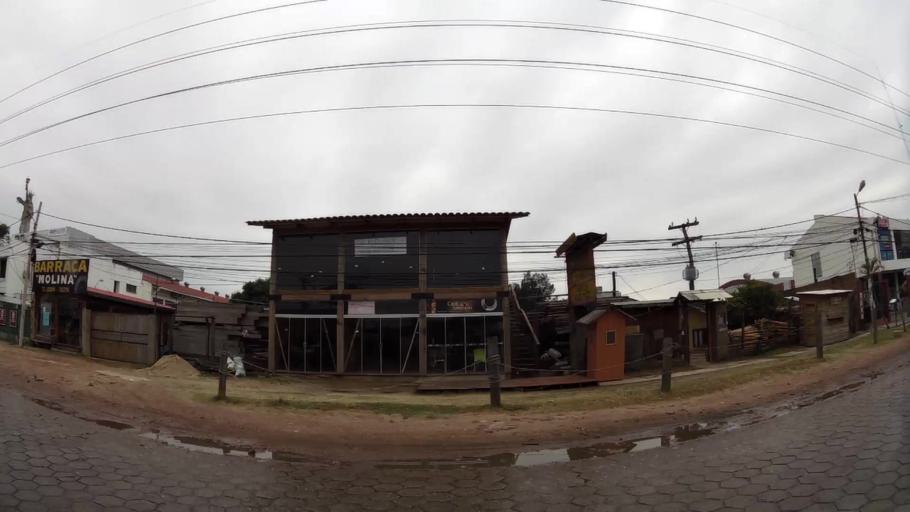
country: BO
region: Santa Cruz
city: Santa Cruz de la Sierra
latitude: -17.7595
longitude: -63.1770
